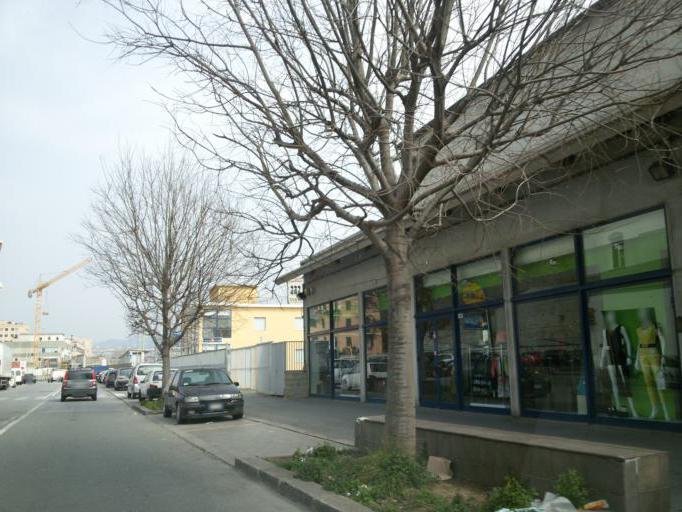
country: IT
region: Liguria
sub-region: Provincia di Genova
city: San Teodoro
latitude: 44.4176
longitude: 8.8778
